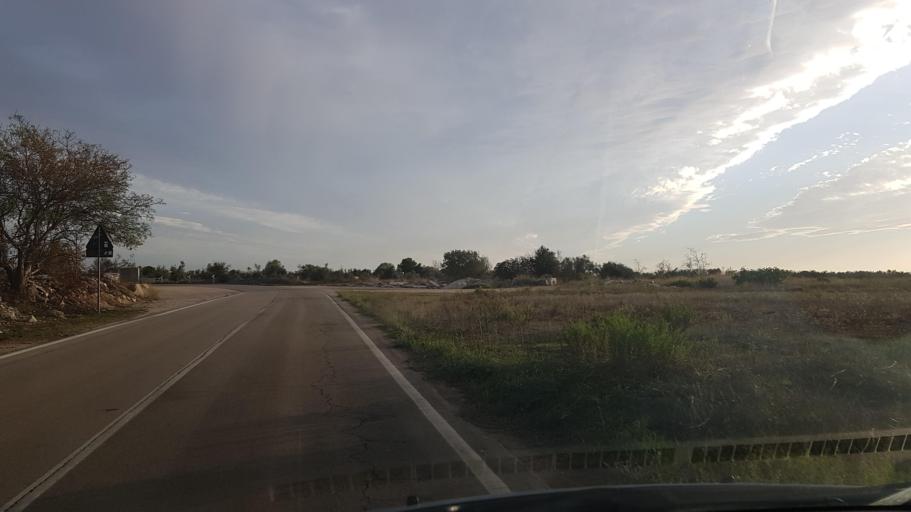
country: IT
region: Apulia
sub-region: Provincia di Lecce
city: Surbo
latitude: 40.4224
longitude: 18.1200
